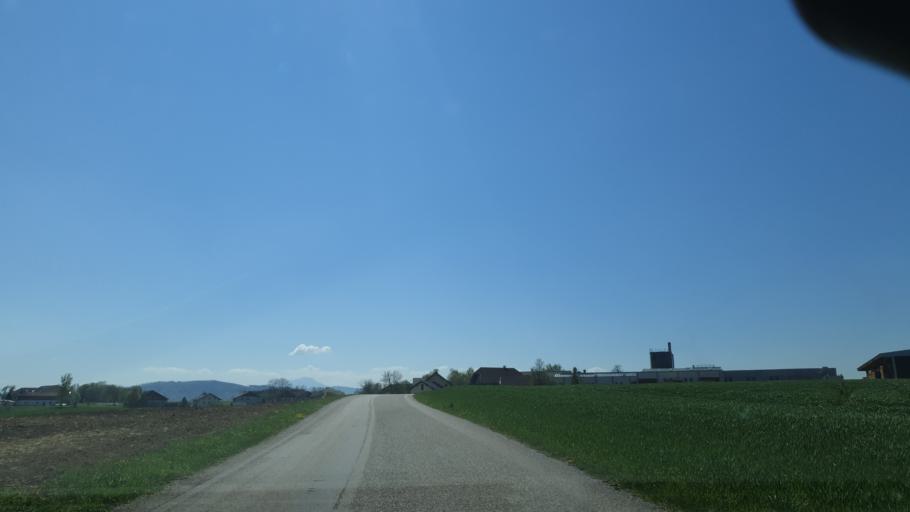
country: AT
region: Upper Austria
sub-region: Politischer Bezirk Vocklabruck
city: Gampern
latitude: 47.9813
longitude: 13.5472
